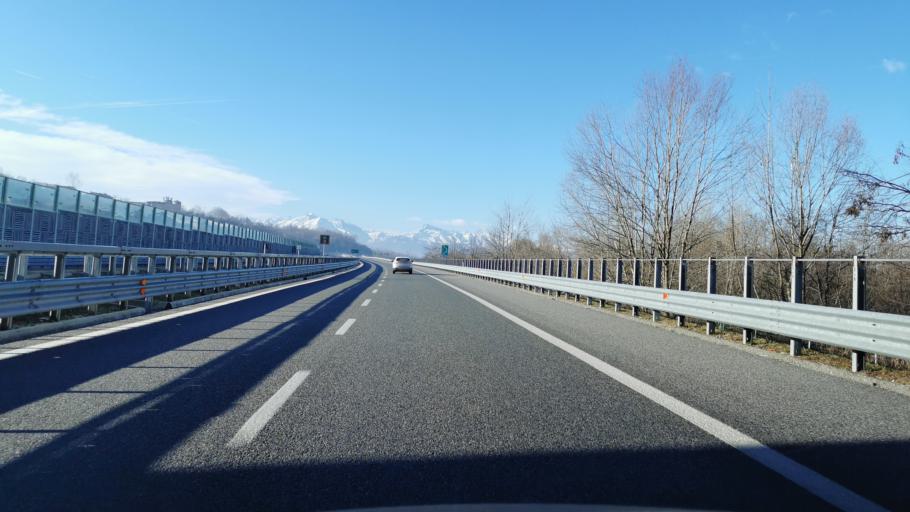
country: IT
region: Piedmont
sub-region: Provincia di Cuneo
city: Castelletto Stura
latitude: 44.4475
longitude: 7.6386
